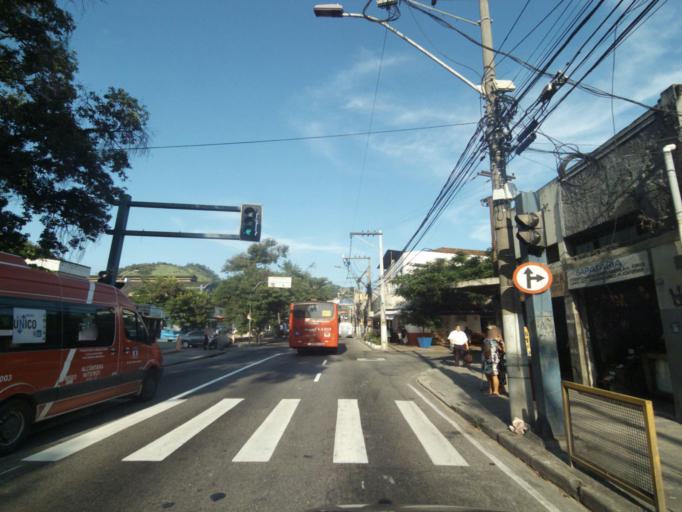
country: BR
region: Rio de Janeiro
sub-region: Niteroi
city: Niteroi
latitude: -22.8816
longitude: -43.0812
